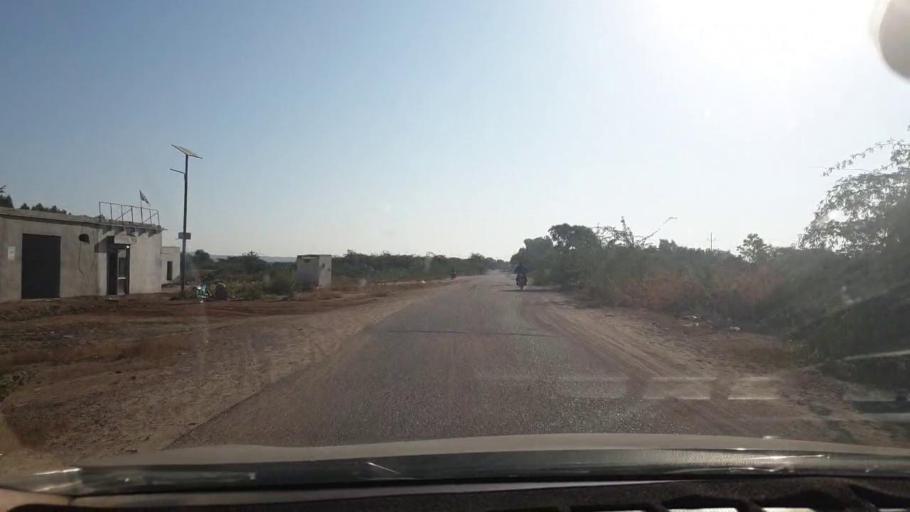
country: PK
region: Sindh
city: Malir Cantonment
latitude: 25.1760
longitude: 67.2046
